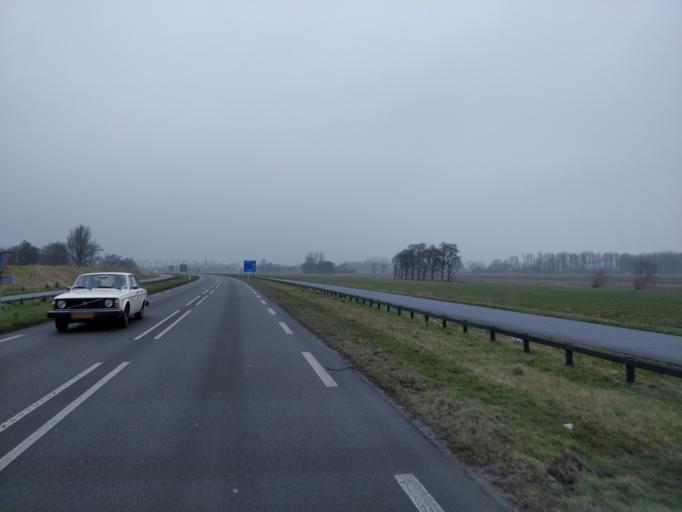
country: NL
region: Friesland
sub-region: Menameradiel
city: Marsum
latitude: 53.2268
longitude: 5.6982
